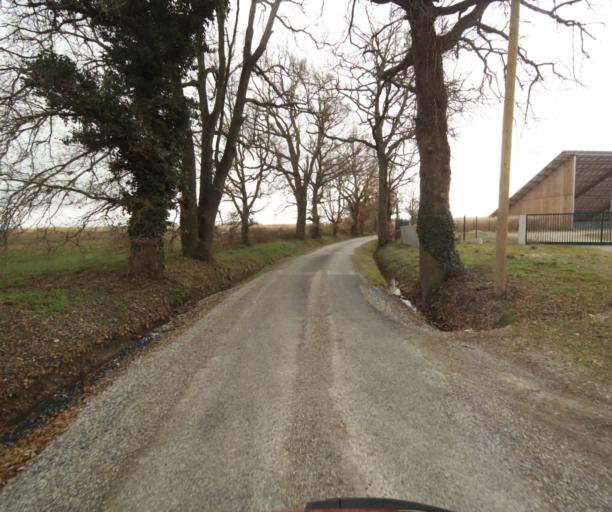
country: FR
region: Midi-Pyrenees
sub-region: Departement de l'Ariege
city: Mazeres
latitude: 43.1993
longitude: 1.6717
